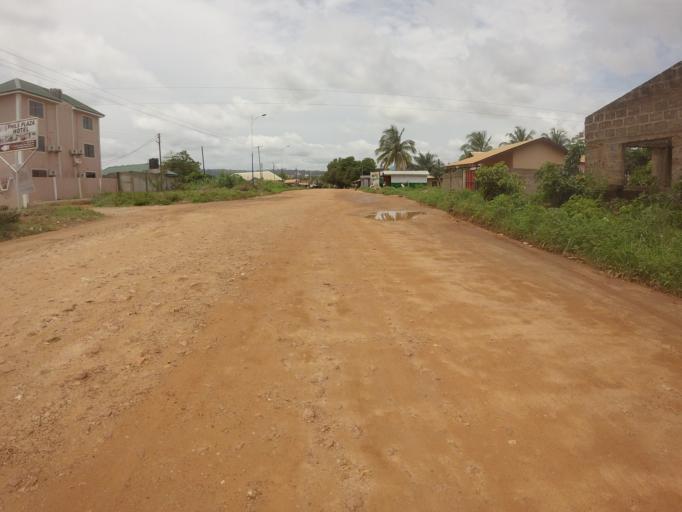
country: GH
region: Volta
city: Ho
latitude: 6.5815
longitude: 0.4631
